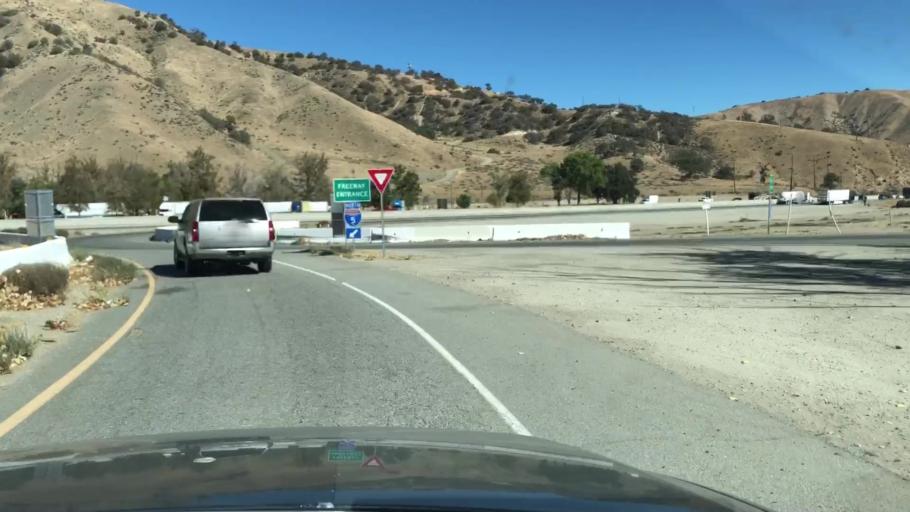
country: US
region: California
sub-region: Kern County
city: Lebec
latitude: 34.8266
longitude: -118.8710
